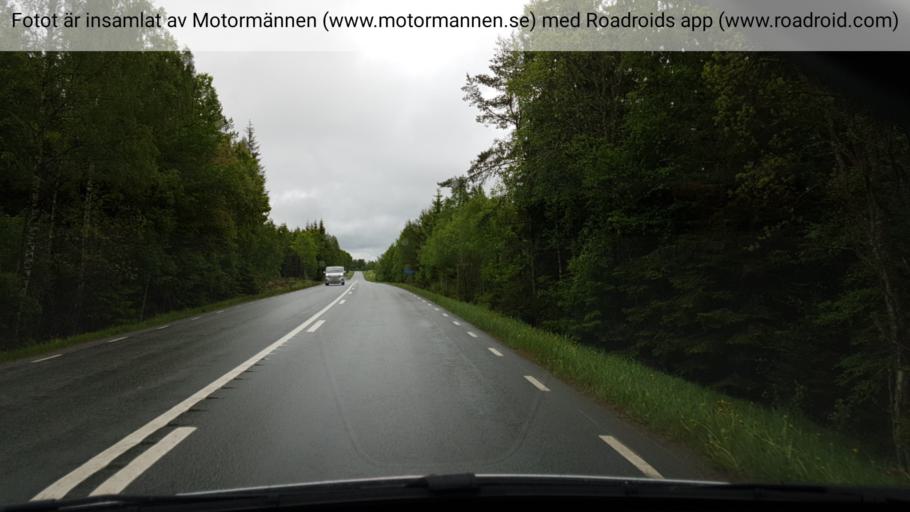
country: SE
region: Joenkoeping
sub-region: Aneby Kommun
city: Hestra
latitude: 57.7724
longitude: 14.4860
